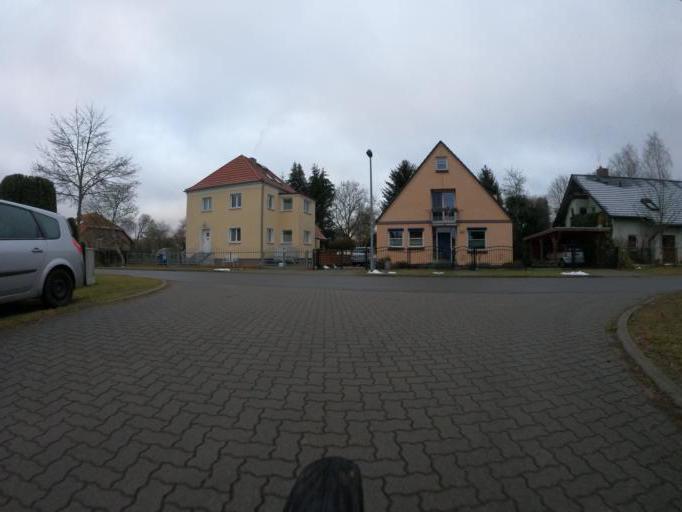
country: DE
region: Brandenburg
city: Schulzendorf
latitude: 52.3630
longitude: 13.5961
